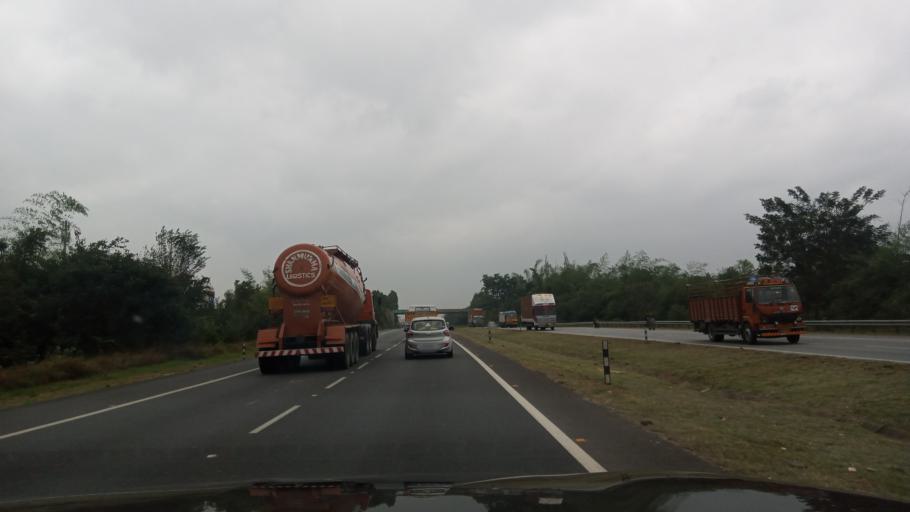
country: IN
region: Karnataka
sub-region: Bangalore Rural
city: Nelamangala
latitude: 13.0288
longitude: 77.4755
